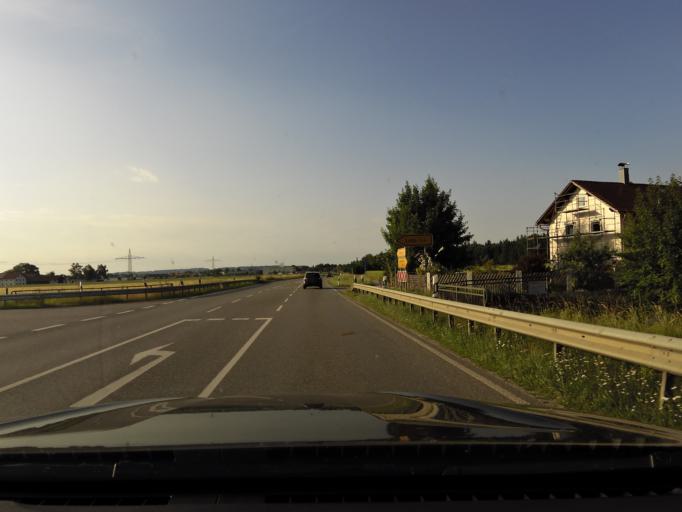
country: DE
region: Bavaria
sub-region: Upper Bavaria
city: Kastl
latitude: 48.2126
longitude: 12.6943
